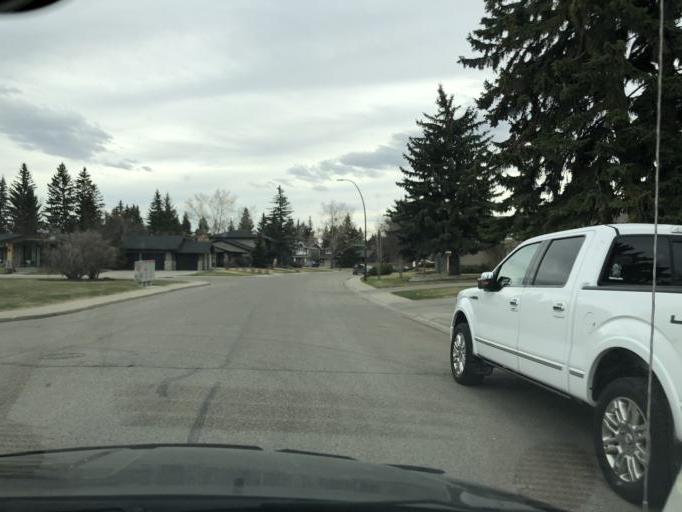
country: CA
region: Alberta
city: Calgary
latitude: 50.9417
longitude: -114.0572
